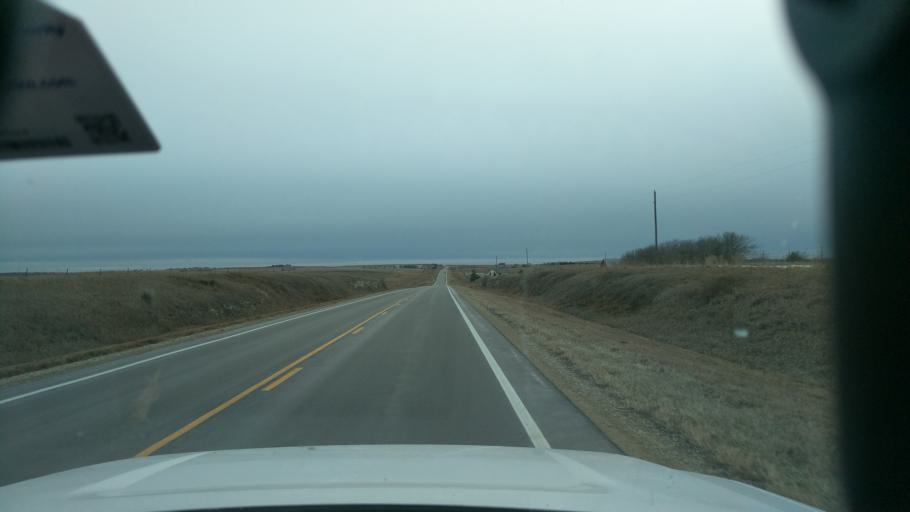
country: US
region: Kansas
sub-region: Dickinson County
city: Herington
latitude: 38.7685
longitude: -96.9273
